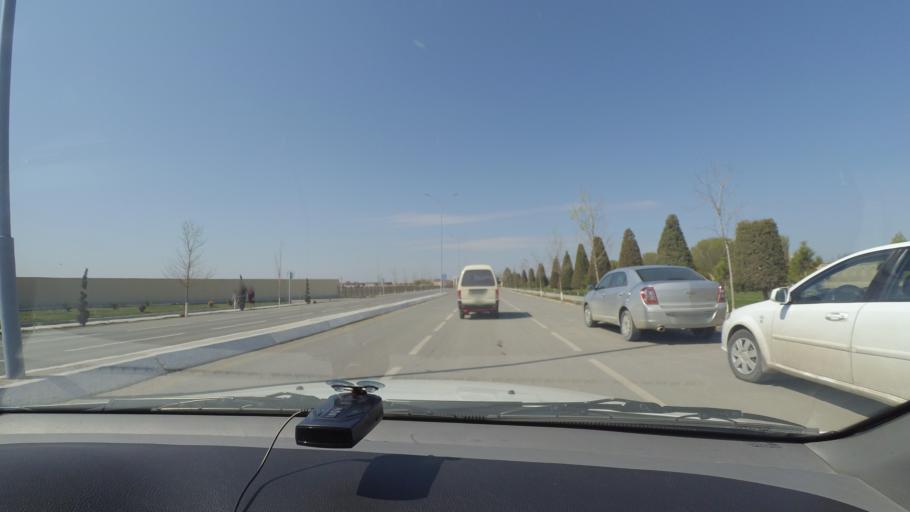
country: UZ
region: Bukhara
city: Kogon
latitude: 39.8001
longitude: 64.5365
